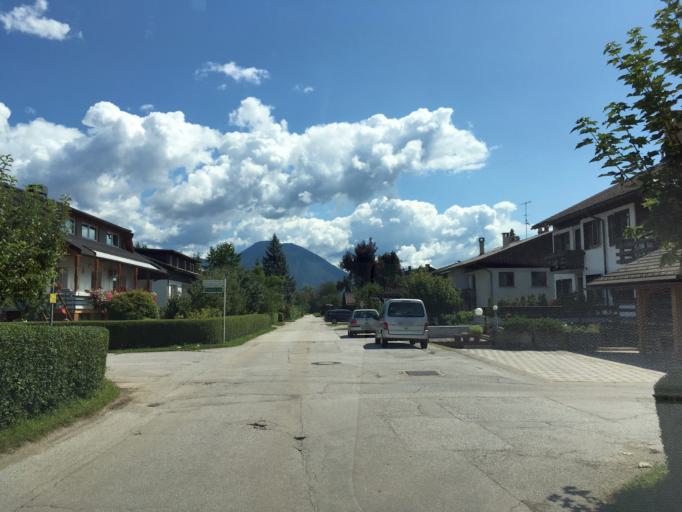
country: SI
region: Bled
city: Bled
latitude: 46.3705
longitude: 14.1226
